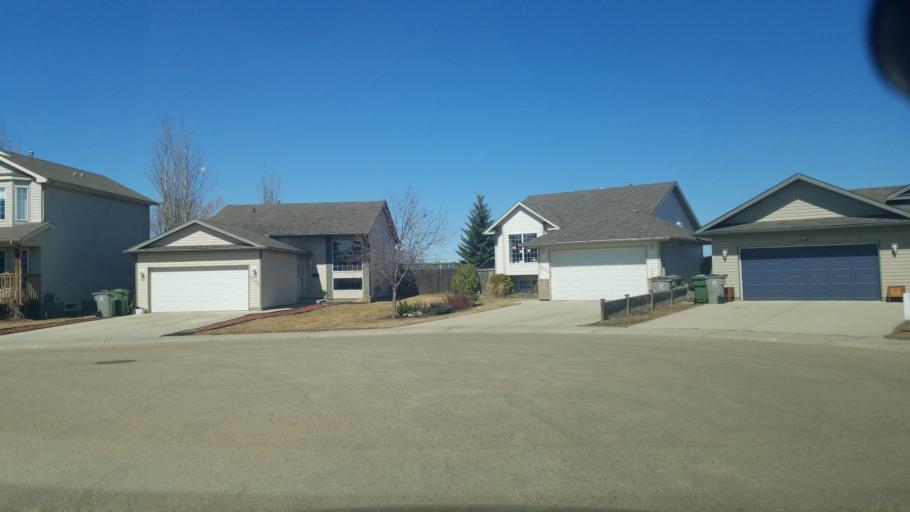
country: CA
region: Saskatchewan
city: Lloydminster
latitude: 53.2579
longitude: -110.0085
